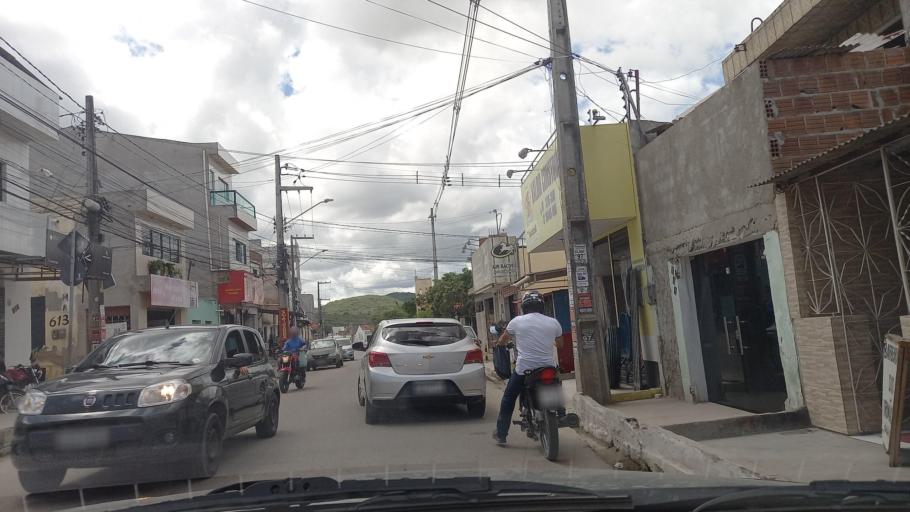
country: BR
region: Pernambuco
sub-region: Caruaru
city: Caruaru
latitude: -8.2796
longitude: -35.9458
